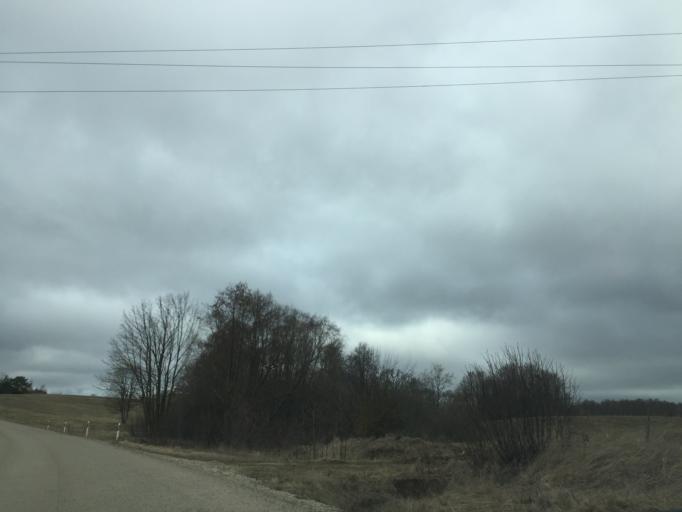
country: LV
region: Ilukste
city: Ilukste
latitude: 56.0417
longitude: 26.2004
